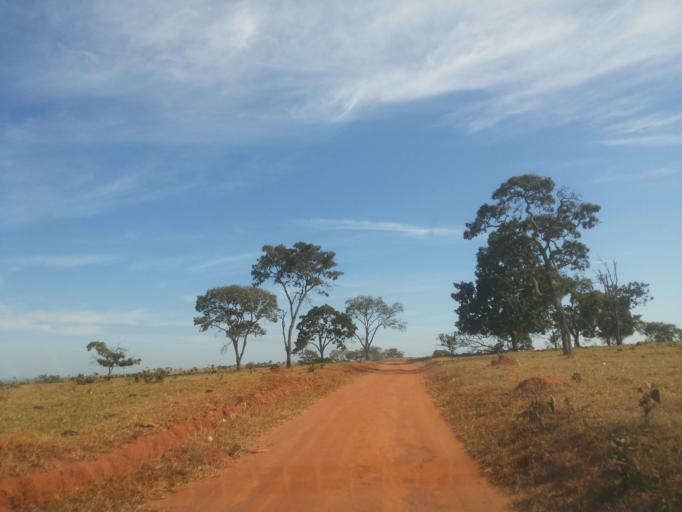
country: BR
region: Minas Gerais
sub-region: Ituiutaba
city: Ituiutaba
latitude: -19.1136
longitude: -49.4103
